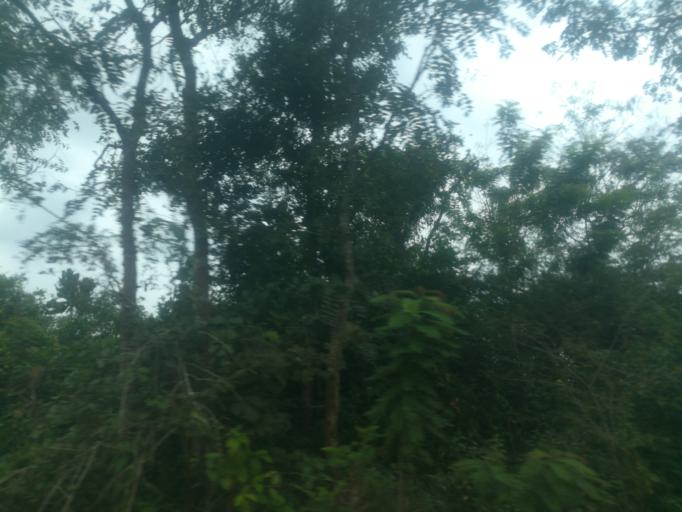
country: NG
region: Ogun
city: Itori
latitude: 7.1001
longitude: 3.1576
